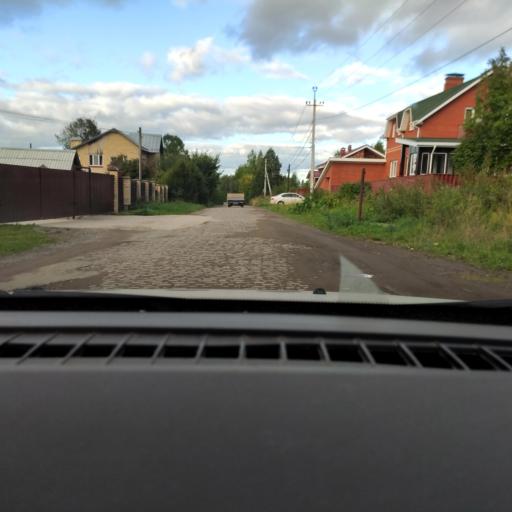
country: RU
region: Perm
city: Perm
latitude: 58.1124
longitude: 56.3884
